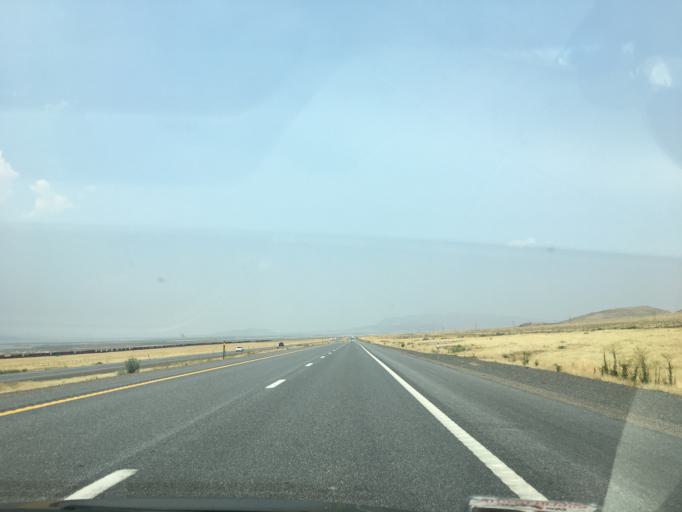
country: US
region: Nevada
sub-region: Pershing County
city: Lovelock
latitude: 40.5382
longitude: -118.2781
